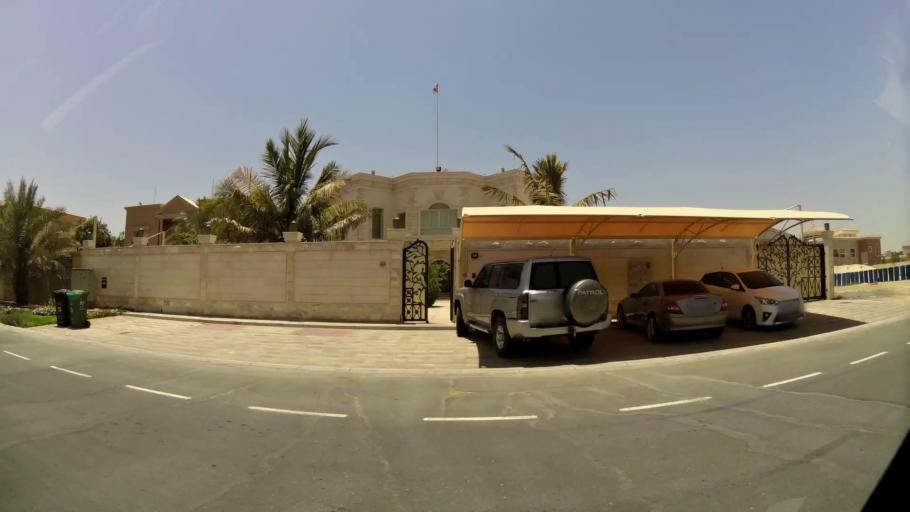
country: AE
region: Dubai
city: Dubai
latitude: 25.0897
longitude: 55.1991
